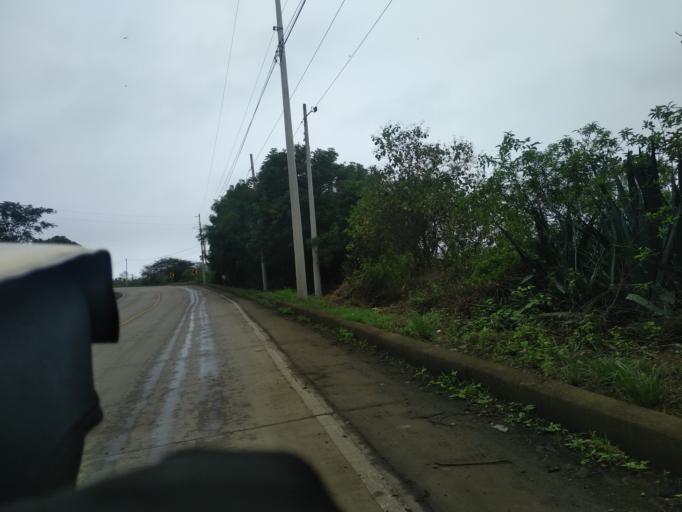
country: EC
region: Manabi
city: Pajan
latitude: -1.6798
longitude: -80.8103
